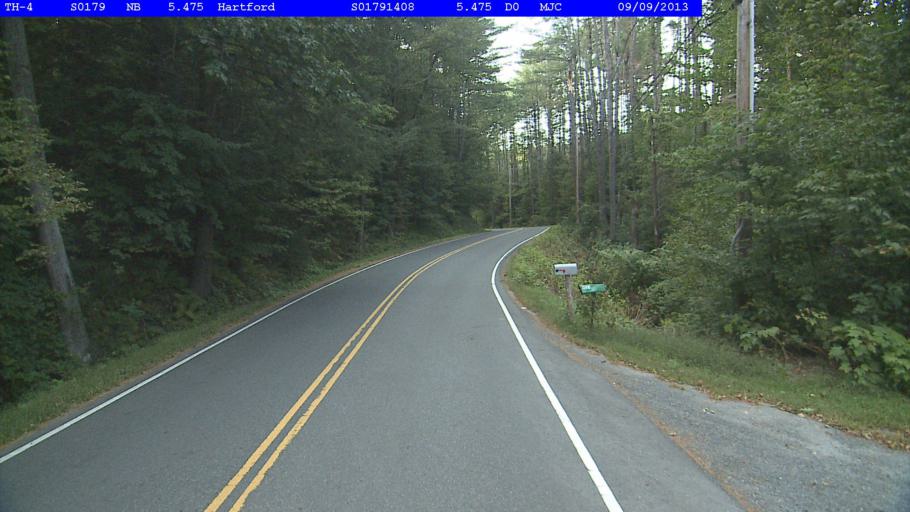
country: US
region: Vermont
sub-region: Windsor County
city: White River Junction
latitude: 43.7069
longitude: -72.4219
